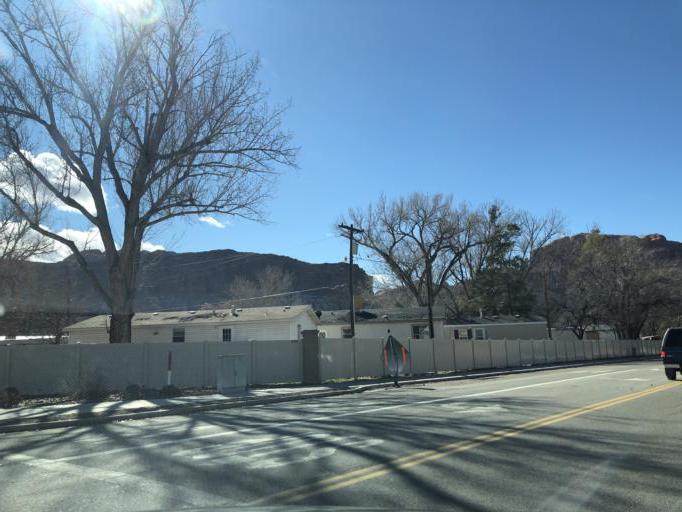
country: US
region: Utah
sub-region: Grand County
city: Moab
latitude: 38.5794
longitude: -109.5613
